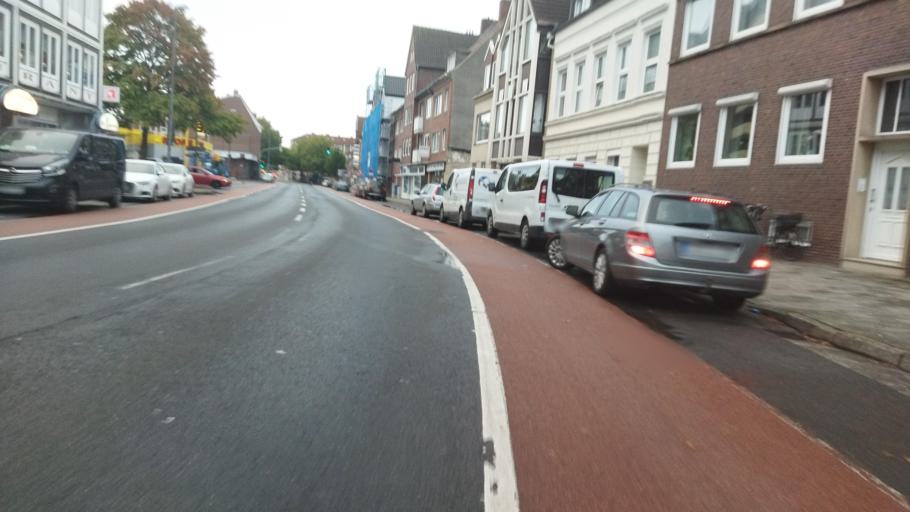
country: DE
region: Lower Saxony
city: Emden
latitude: 53.3727
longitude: 7.2063
